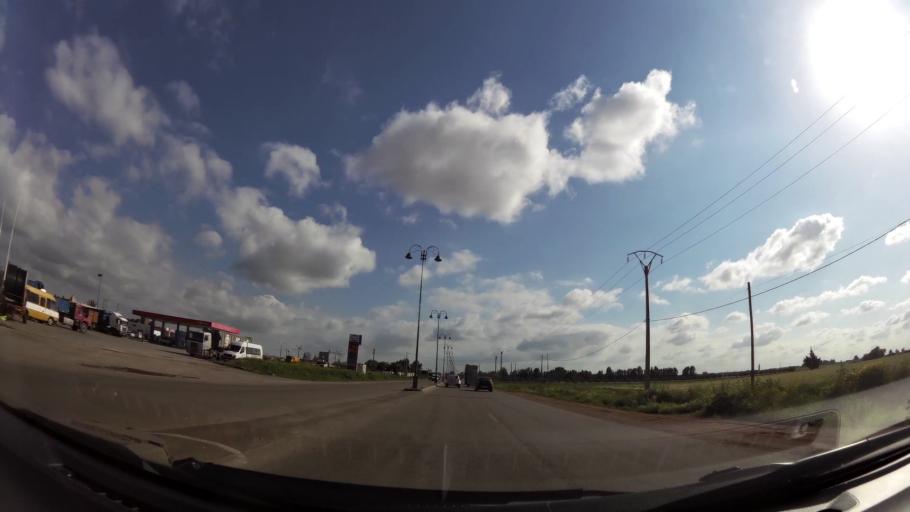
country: MA
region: Chaouia-Ouardigha
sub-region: Settat Province
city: Berrechid
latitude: 33.2903
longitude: -7.5761
